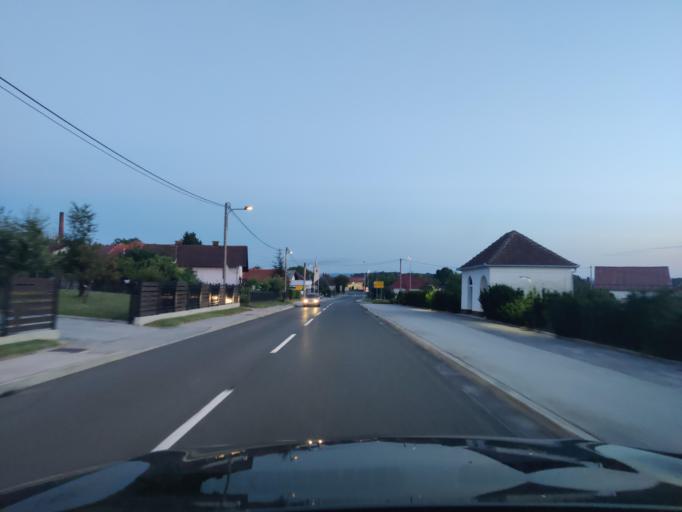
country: SI
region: Lendava-Lendva
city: Lendava
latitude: 46.5841
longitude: 16.4484
